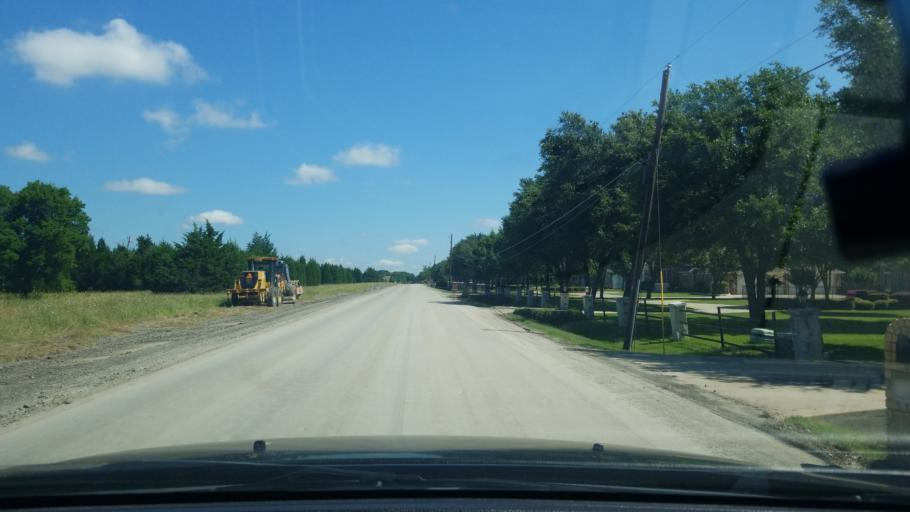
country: US
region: Texas
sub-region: Dallas County
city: Sunnyvale
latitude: 32.7900
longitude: -96.5797
